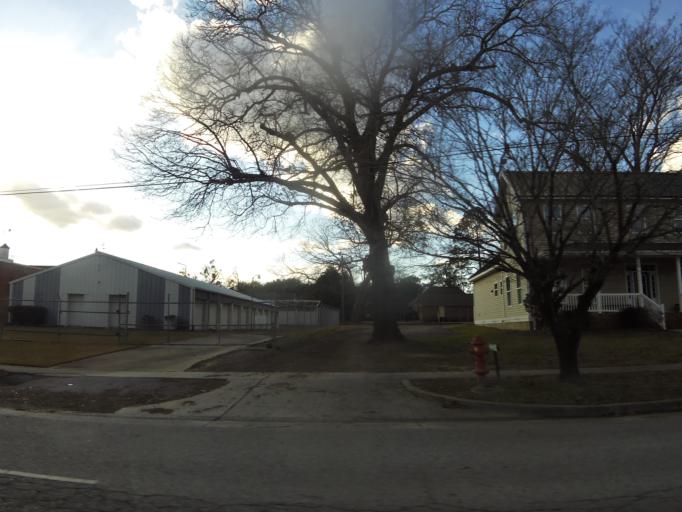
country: US
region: South Carolina
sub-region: Clarendon County
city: Manning
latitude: 33.6983
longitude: -80.2091
